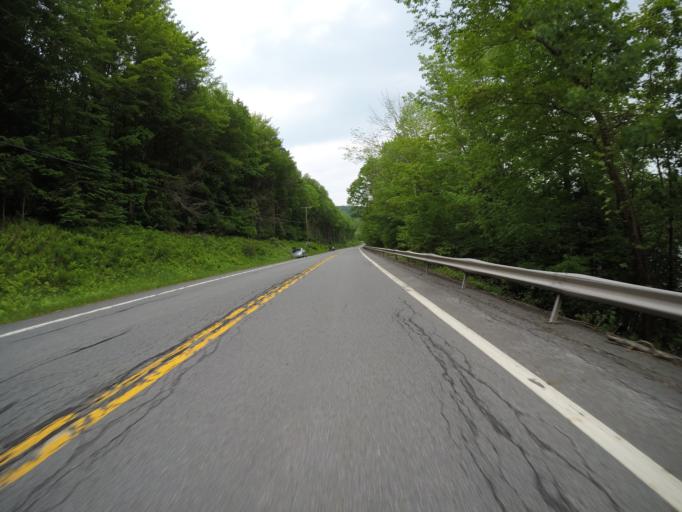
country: US
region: New York
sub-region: Sullivan County
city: Livingston Manor
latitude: 42.0722
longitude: -74.9120
